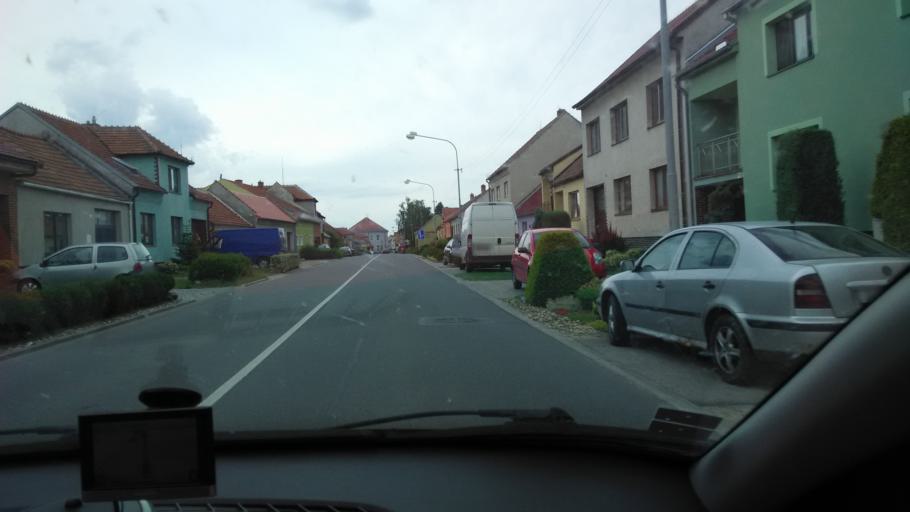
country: CZ
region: South Moravian
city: Kostice
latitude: 48.7498
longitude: 16.9837
